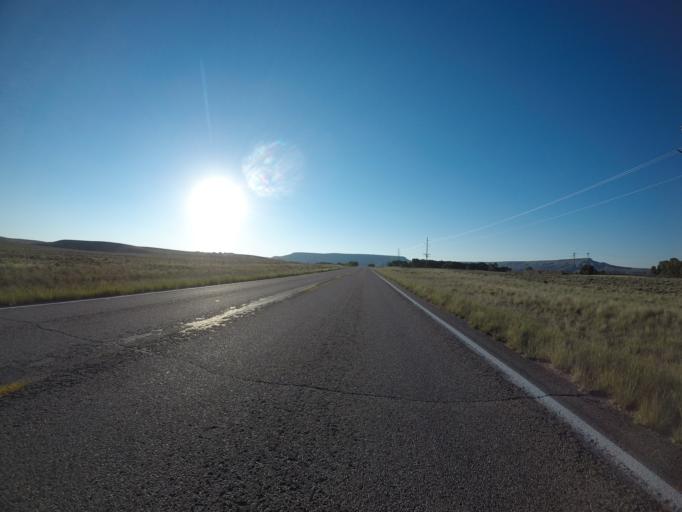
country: US
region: Wyoming
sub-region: Sublette County
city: Marbleton
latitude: 42.5706
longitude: -109.9638
